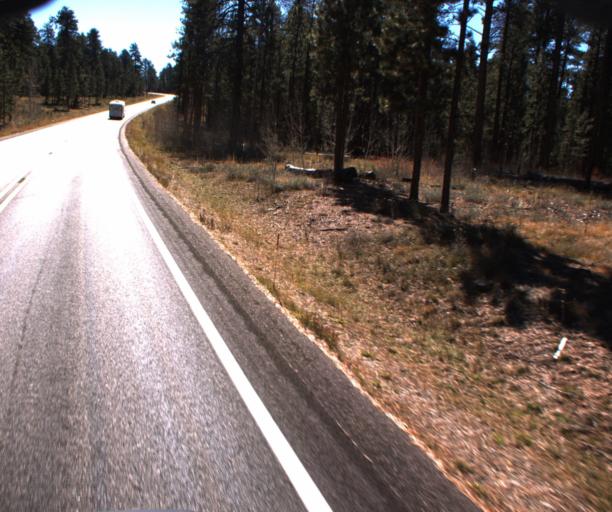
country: US
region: Arizona
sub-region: Coconino County
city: Fredonia
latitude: 36.6516
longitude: -112.1840
